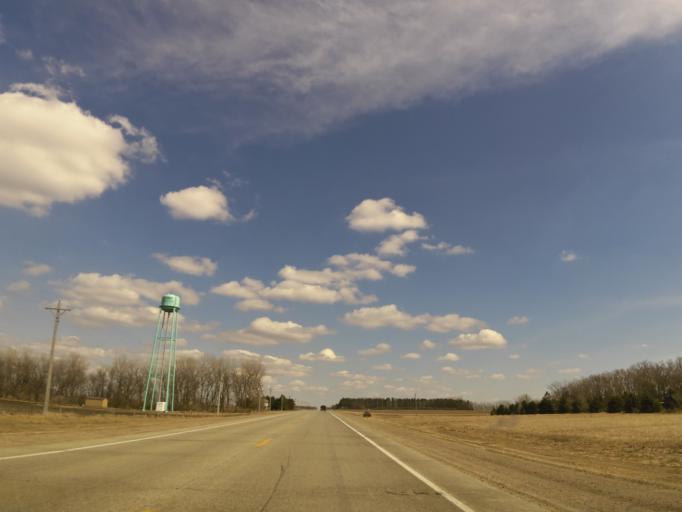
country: US
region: South Dakota
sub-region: Codington County
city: Watertown
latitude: 44.8902
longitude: -96.9691
